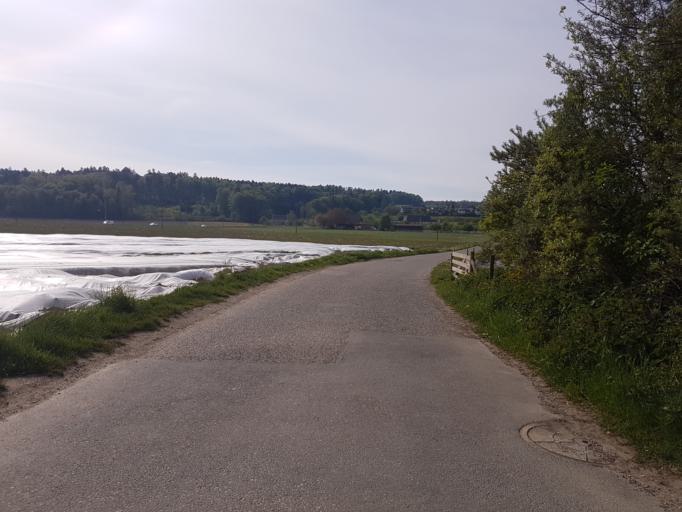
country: CH
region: Bern
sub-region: Seeland District
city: Tauffelen
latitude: 47.0931
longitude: 7.2116
